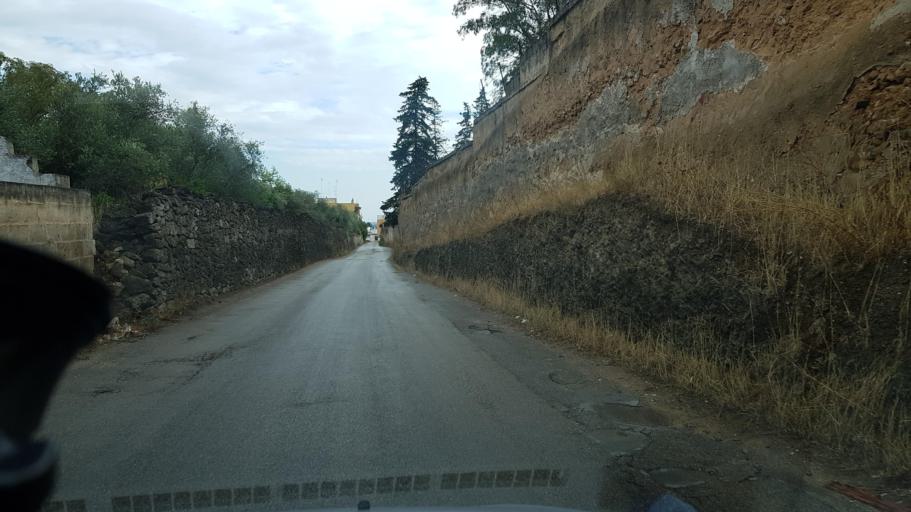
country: IT
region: Apulia
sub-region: Provincia di Brindisi
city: Oria
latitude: 40.4985
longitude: 17.6520
